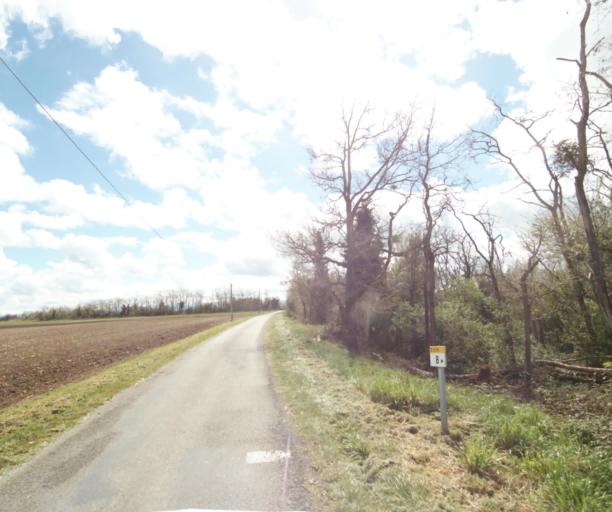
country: FR
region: Midi-Pyrenees
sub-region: Departement de l'Ariege
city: Saverdun
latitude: 43.2703
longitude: 1.5826
